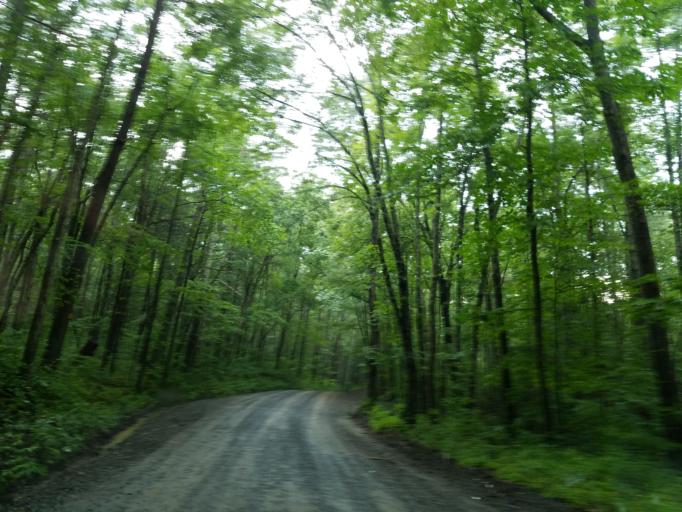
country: US
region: Georgia
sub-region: Fannin County
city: Blue Ridge
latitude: 34.7808
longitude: -84.3322
